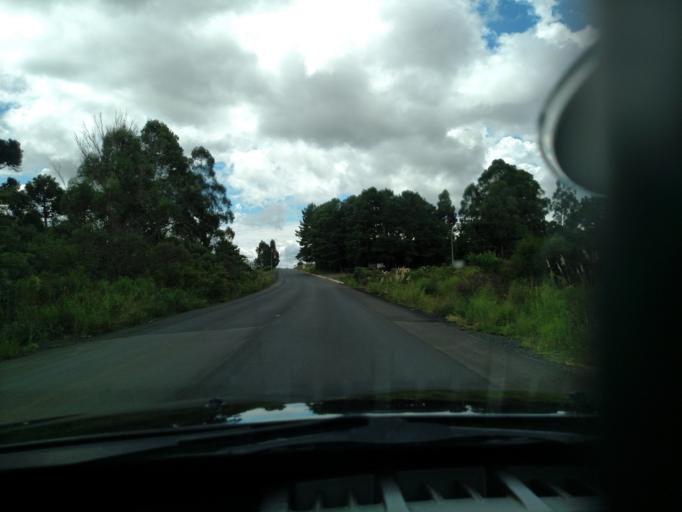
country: BR
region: Santa Catarina
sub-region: Lages
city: Lages
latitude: -27.9472
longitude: -50.0955
